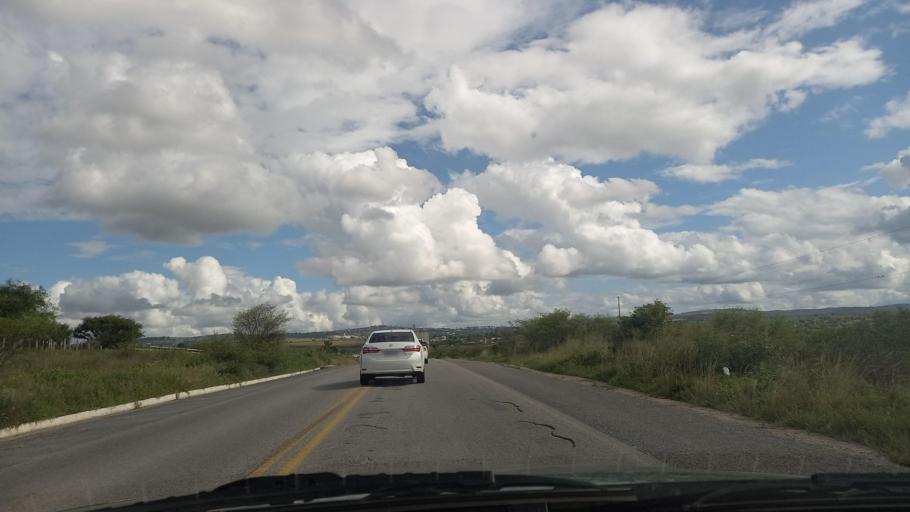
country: BR
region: Pernambuco
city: Garanhuns
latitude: -8.8191
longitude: -36.4481
